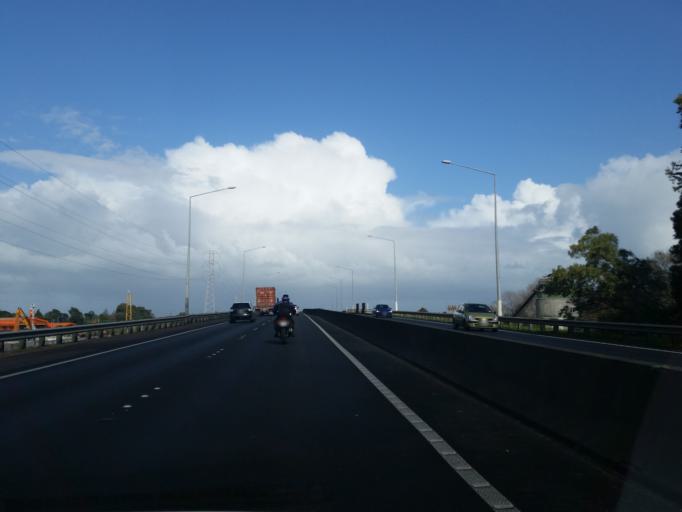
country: NZ
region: Auckland
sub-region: Auckland
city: Takanini
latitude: -37.0328
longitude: 174.9101
